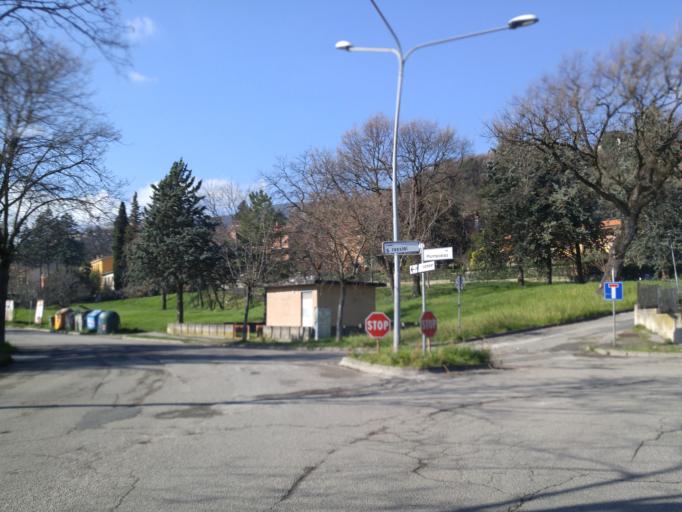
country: IT
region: The Marches
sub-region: Provincia di Pesaro e Urbino
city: Fossombrone
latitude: 43.6947
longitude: 12.8195
